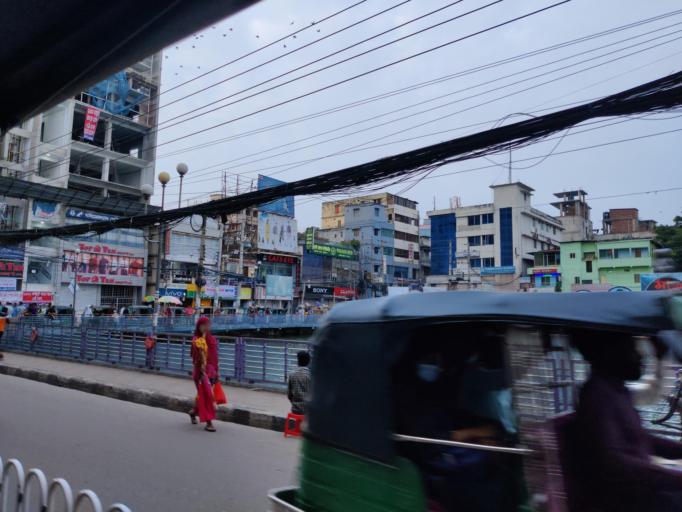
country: BD
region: Barisal
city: Barisal
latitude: 22.7034
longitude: 90.3704
